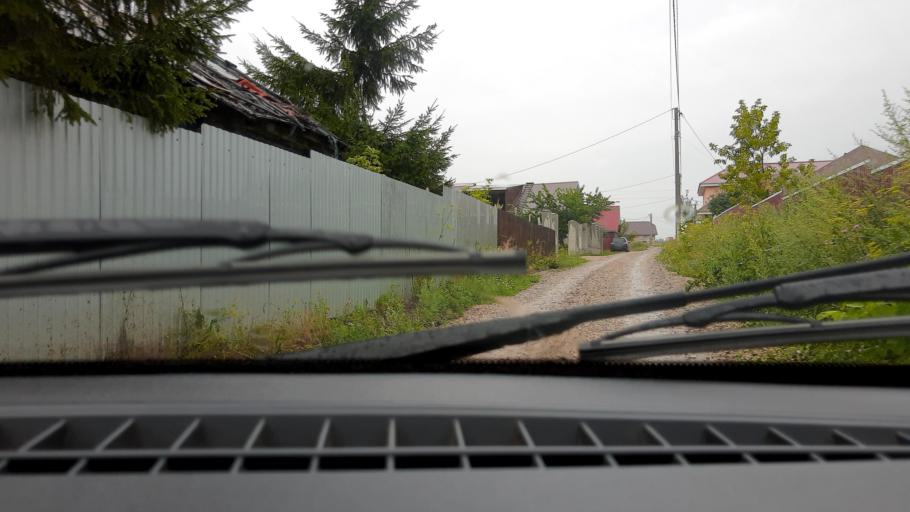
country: RU
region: Bashkortostan
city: Mikhaylovka
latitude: 54.8164
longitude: 55.8486
